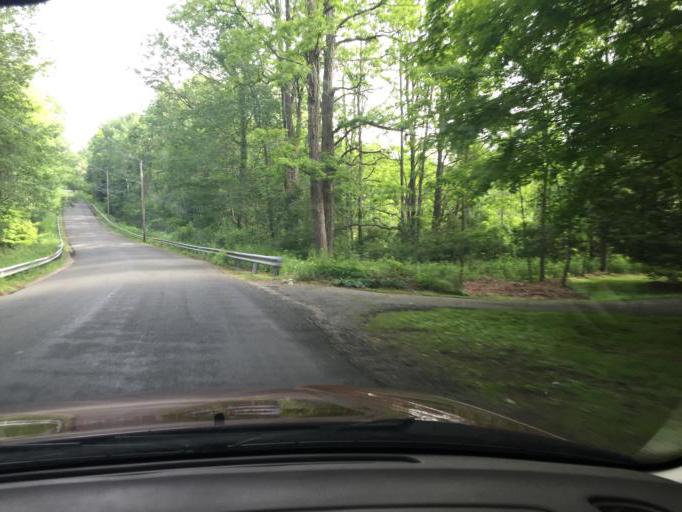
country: US
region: Connecticut
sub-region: Litchfield County
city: Litchfield
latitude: 41.8068
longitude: -73.2593
